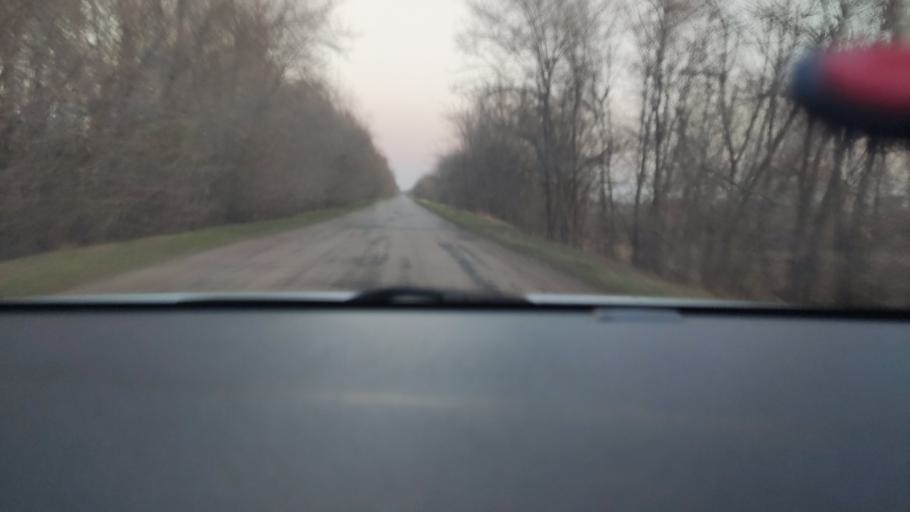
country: RU
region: Voronezj
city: Uryv-Pokrovka
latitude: 51.1336
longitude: 39.0936
